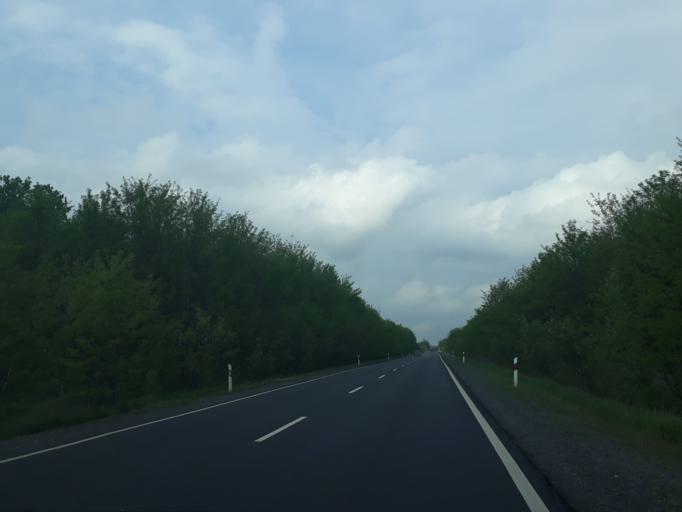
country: HU
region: Szabolcs-Szatmar-Bereg
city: Nyirtass
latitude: 48.1304
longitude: 22.0137
